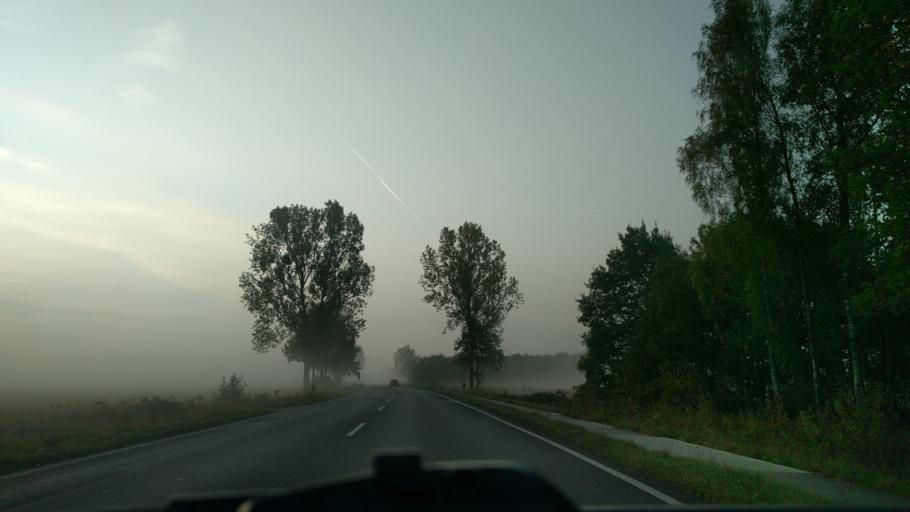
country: DE
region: Lower Saxony
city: Isenbuttel
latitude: 52.4563
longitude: 10.5791
